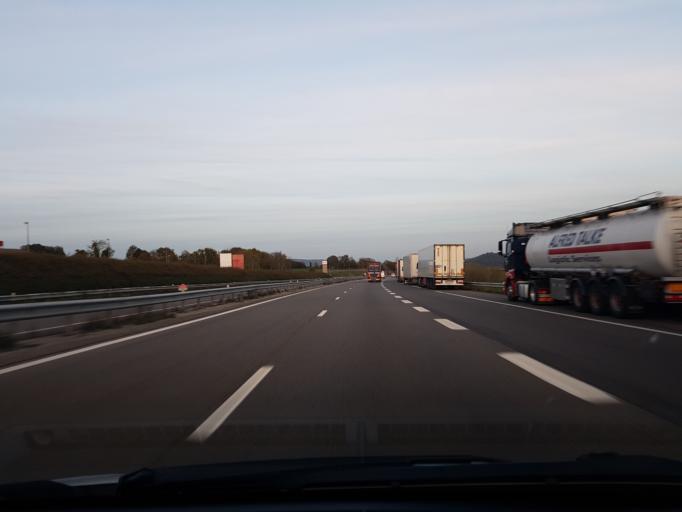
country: FR
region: Franche-Comte
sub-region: Departement du Doubs
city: Novillars
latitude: 47.3289
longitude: 6.1285
